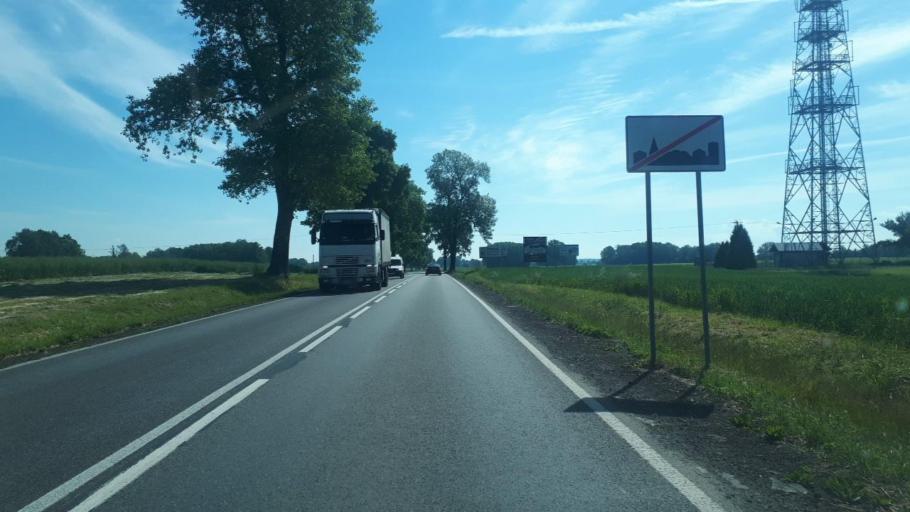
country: PL
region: Silesian Voivodeship
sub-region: Powiat pszczynski
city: Miedzna
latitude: 49.9695
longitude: 19.0555
